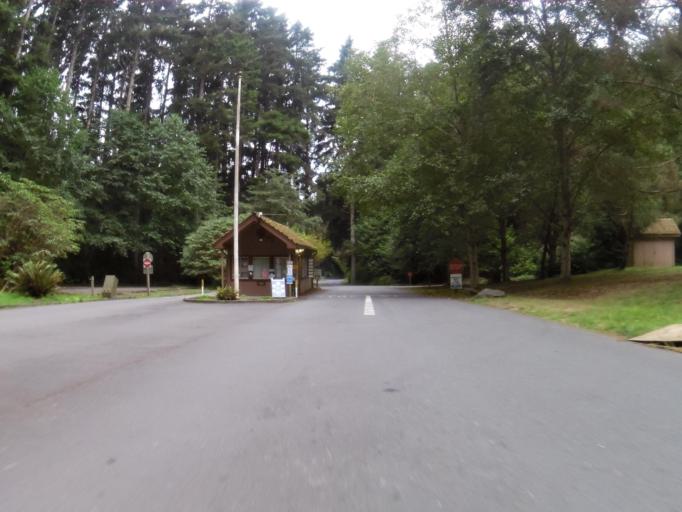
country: US
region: California
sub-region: Humboldt County
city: Westhaven-Moonstone
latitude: 41.1346
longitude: -124.1548
